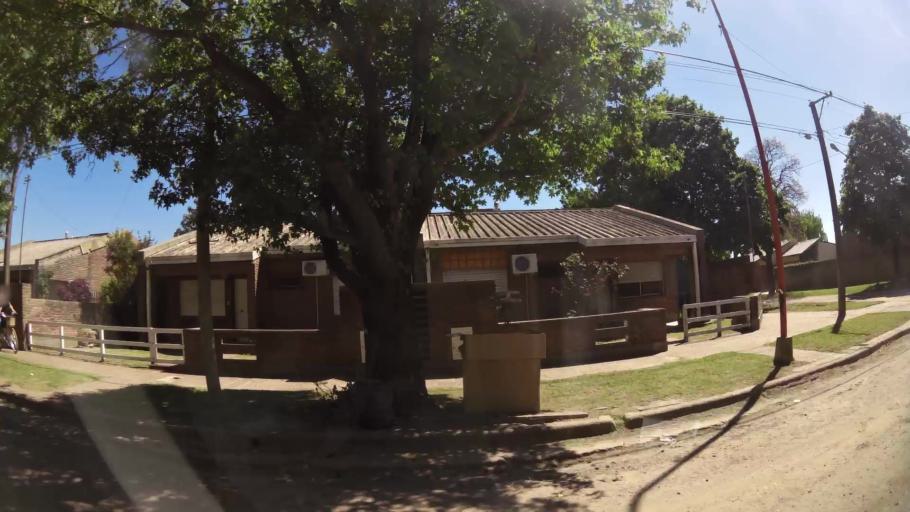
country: AR
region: Santa Fe
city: Esperanza
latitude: -31.4356
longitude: -60.9293
